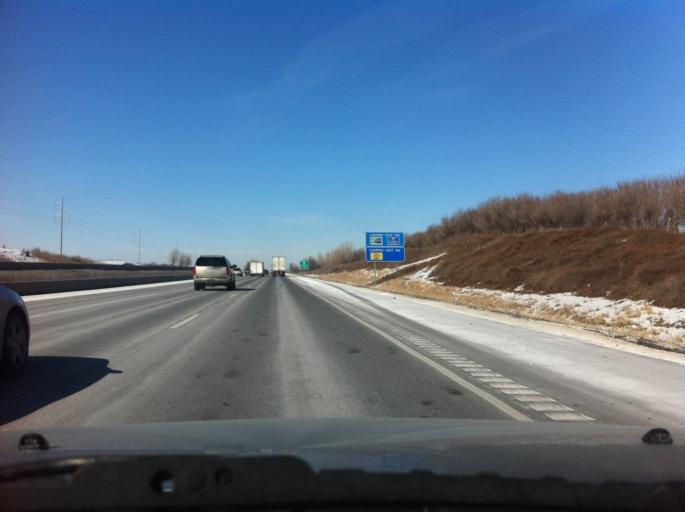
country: US
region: Wisconsin
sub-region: Dane County
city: Windsor
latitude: 43.2227
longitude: -89.3640
